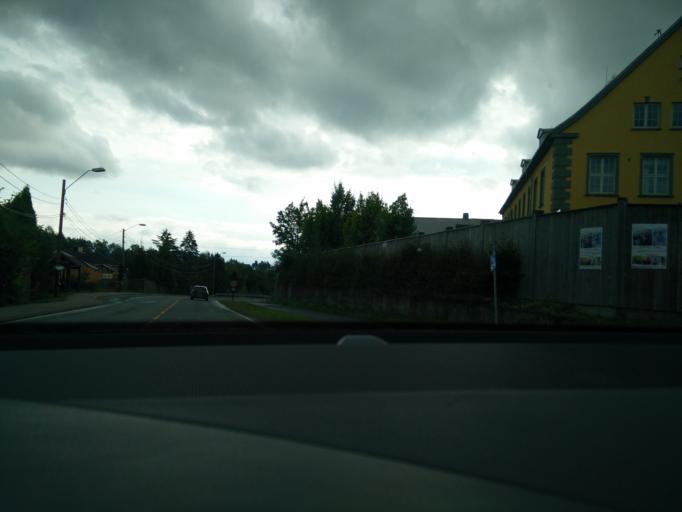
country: NO
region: Akershus
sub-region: Baerum
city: Lysaker
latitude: 59.9208
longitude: 10.6264
